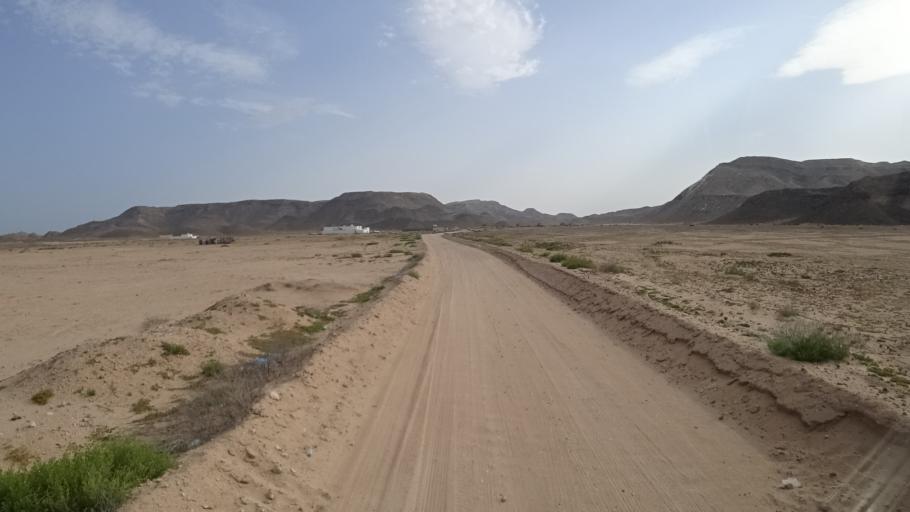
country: OM
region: Ash Sharqiyah
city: Sur
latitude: 22.4415
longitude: 59.8216
